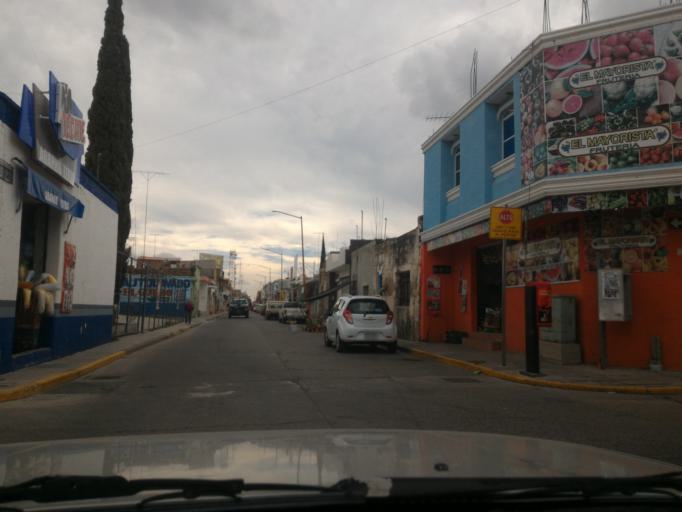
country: MX
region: Guanajuato
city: San Francisco del Rincon
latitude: 21.0229
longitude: -101.8604
